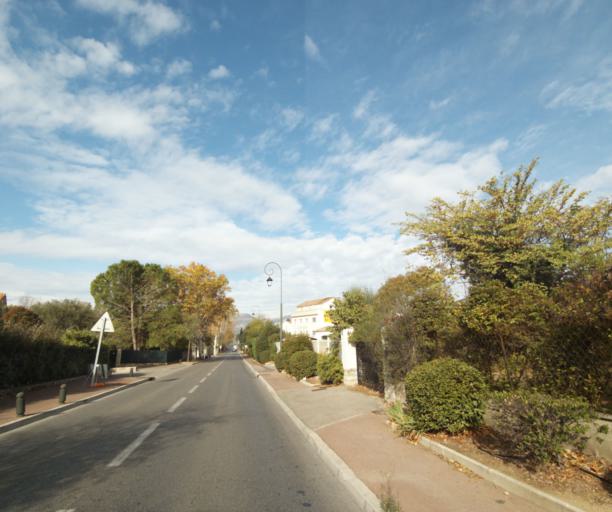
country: FR
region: Provence-Alpes-Cote d'Azur
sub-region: Departement des Bouches-du-Rhone
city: Gemenos
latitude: 43.2982
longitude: 5.6225
